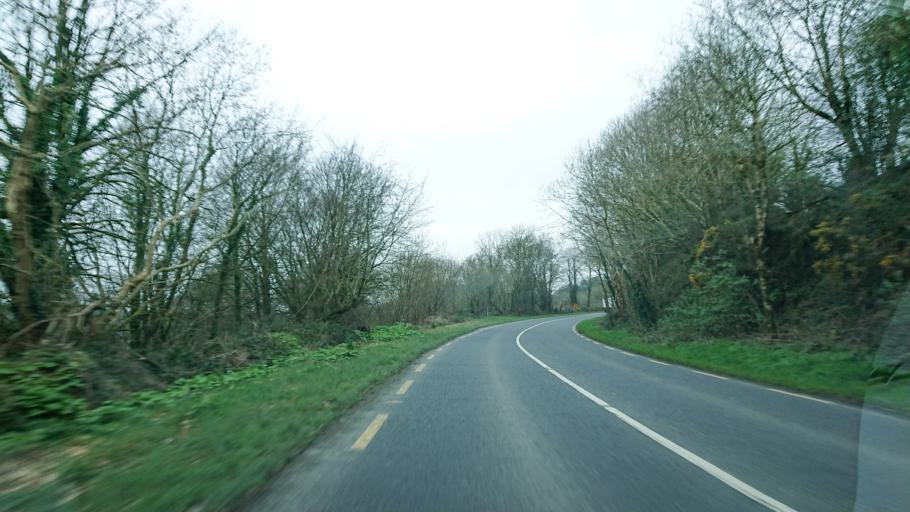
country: IE
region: Munster
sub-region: County Cork
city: Bandon
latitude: 51.7463
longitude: -8.7648
